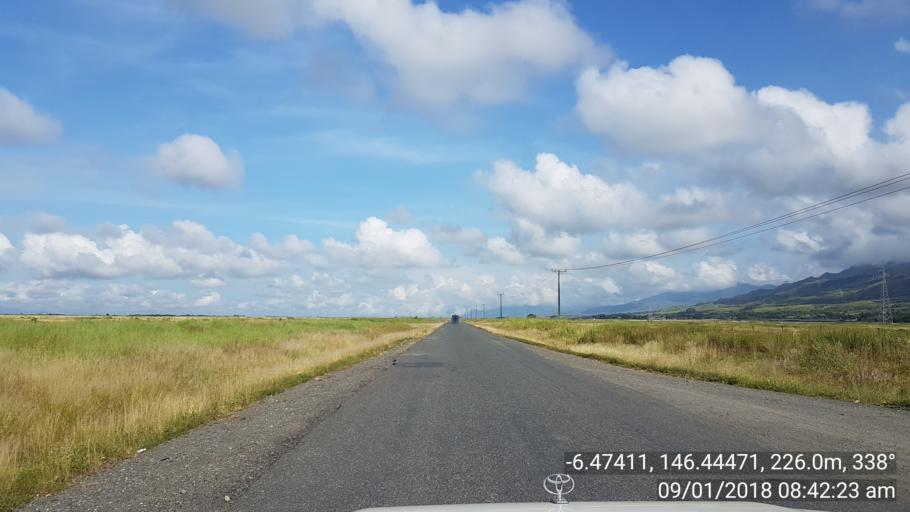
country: PG
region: Morobe
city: Lae
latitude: -6.4742
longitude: 146.4447
